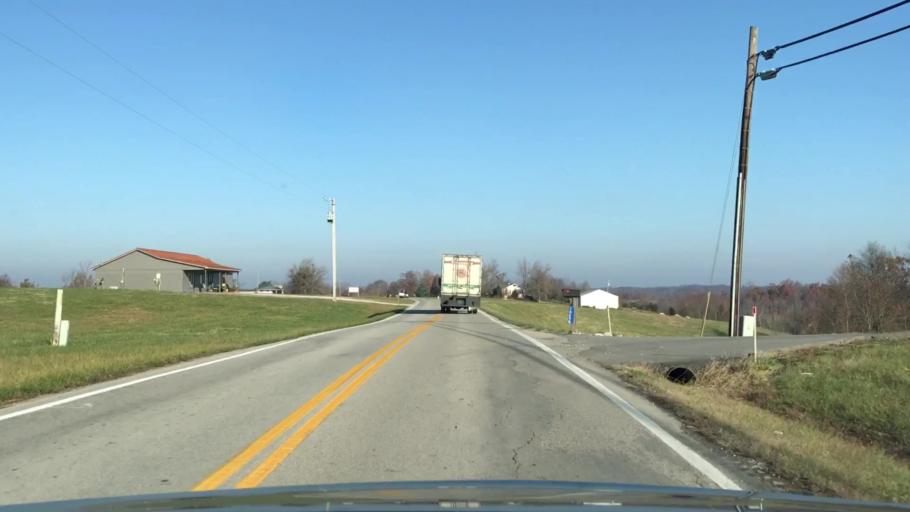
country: US
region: Kentucky
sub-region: Grayson County
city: Leitchfield
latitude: 37.3621
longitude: -86.2418
